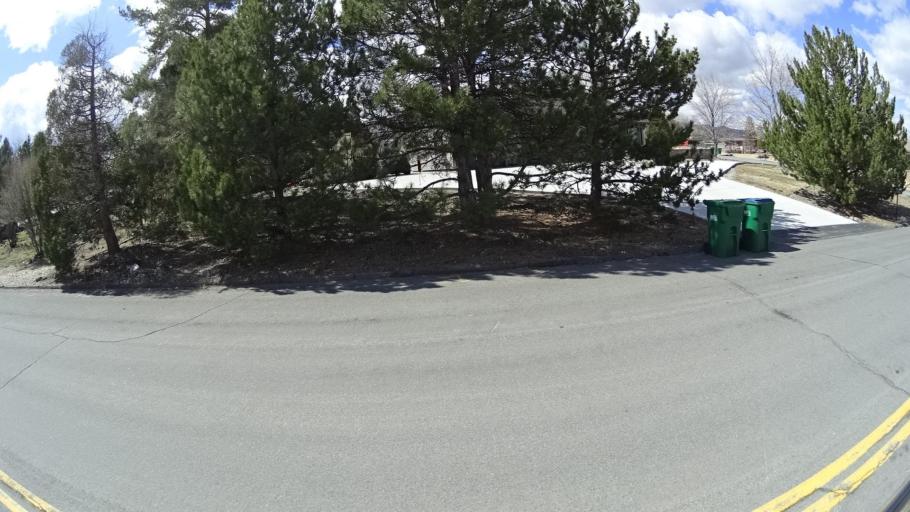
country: US
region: Nevada
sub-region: Washoe County
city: Reno
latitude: 39.4086
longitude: -119.7903
